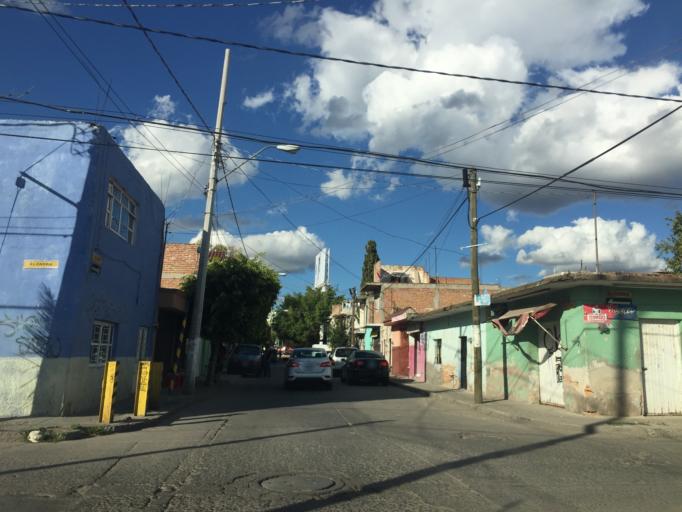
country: MX
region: Guanajuato
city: Leon
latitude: 21.1046
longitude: -101.6995
